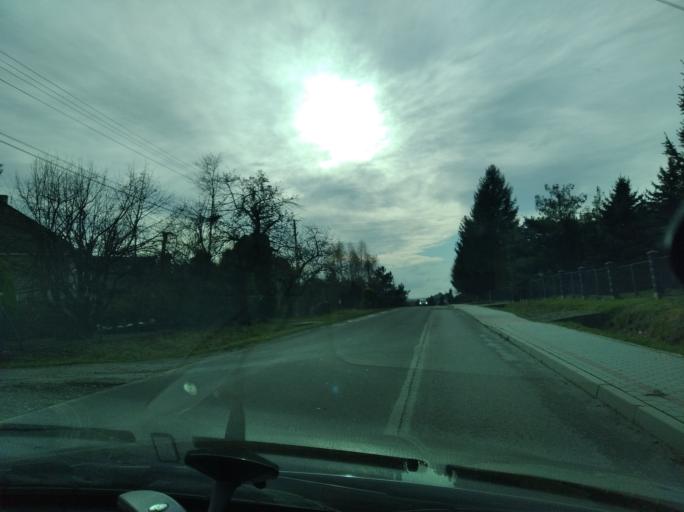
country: PL
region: Subcarpathian Voivodeship
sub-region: Powiat ropczycko-sedziszowski
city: Iwierzyce
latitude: 50.0235
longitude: 21.7546
